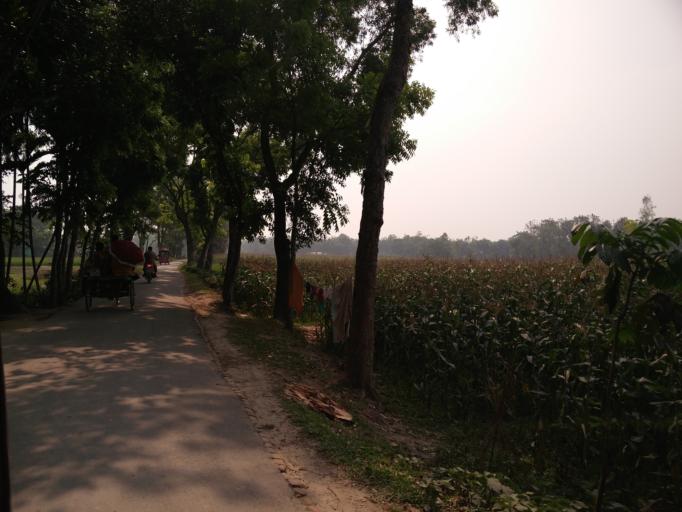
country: BD
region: Dhaka
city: Muktagacha
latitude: 24.9148
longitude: 90.2236
